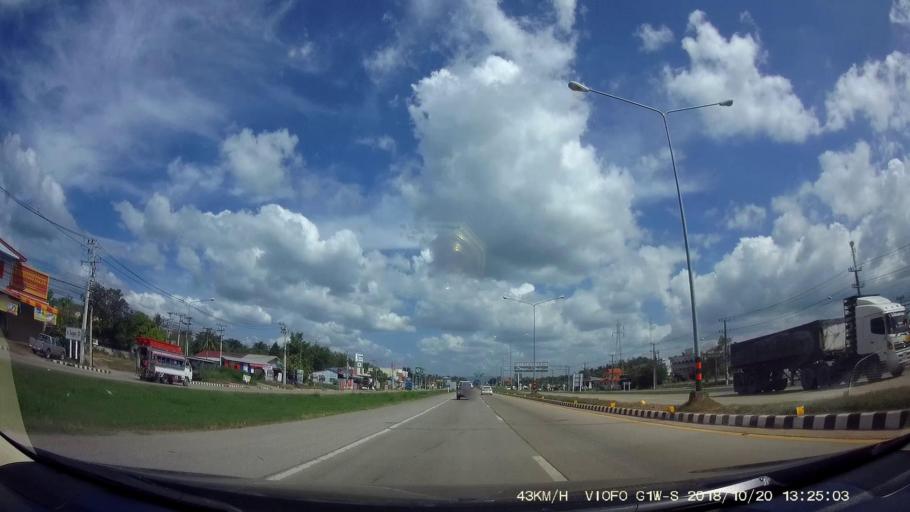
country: TH
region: Chaiyaphum
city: Khon San
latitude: 16.5953
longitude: 101.9280
